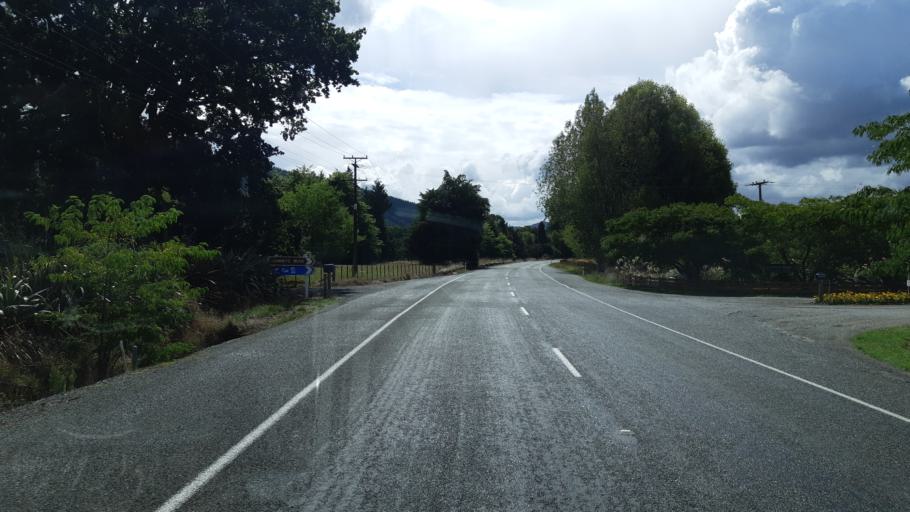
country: NZ
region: Tasman
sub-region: Tasman District
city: Wakefield
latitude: -41.4592
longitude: 172.8115
